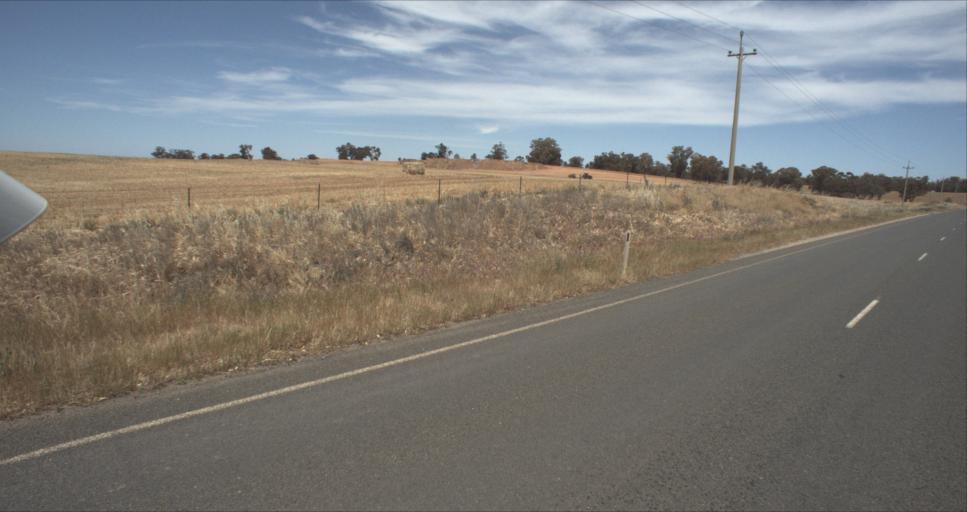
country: AU
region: New South Wales
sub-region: Leeton
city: Leeton
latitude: -34.6555
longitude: 146.4598
